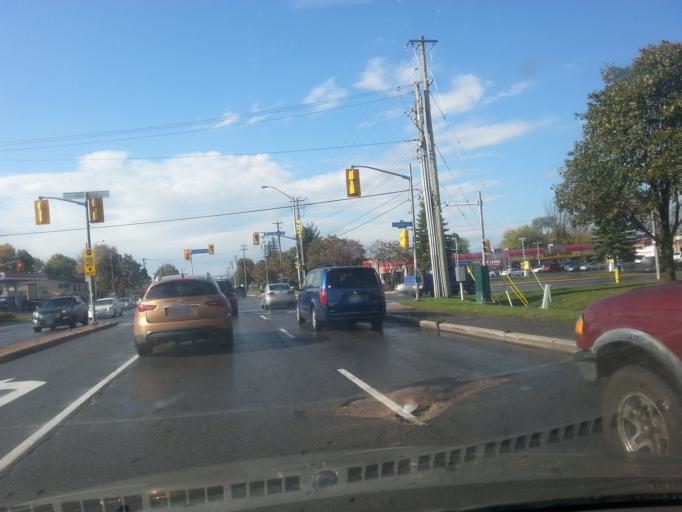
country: CA
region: Ontario
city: Bells Corners
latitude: 45.3280
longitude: -75.8191
